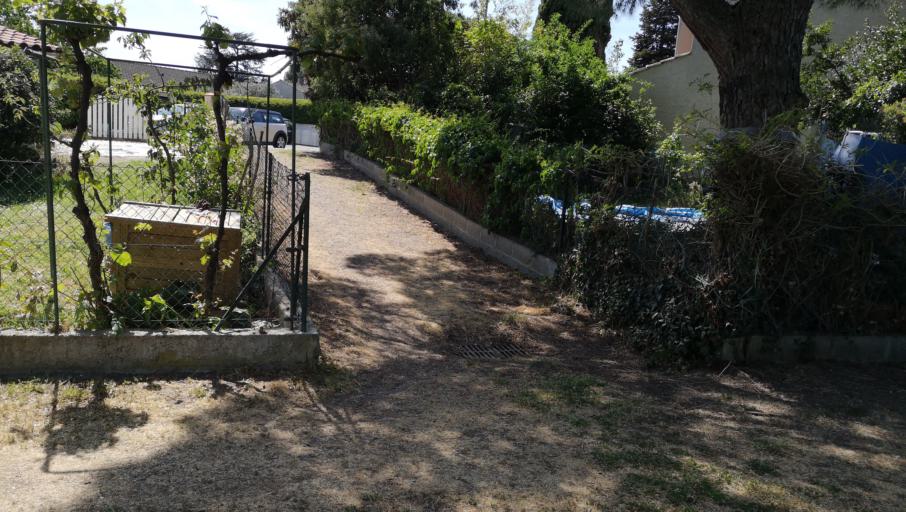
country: FR
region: Midi-Pyrenees
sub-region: Departement de la Haute-Garonne
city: Beauzelle
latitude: 43.6721
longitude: 1.3763
